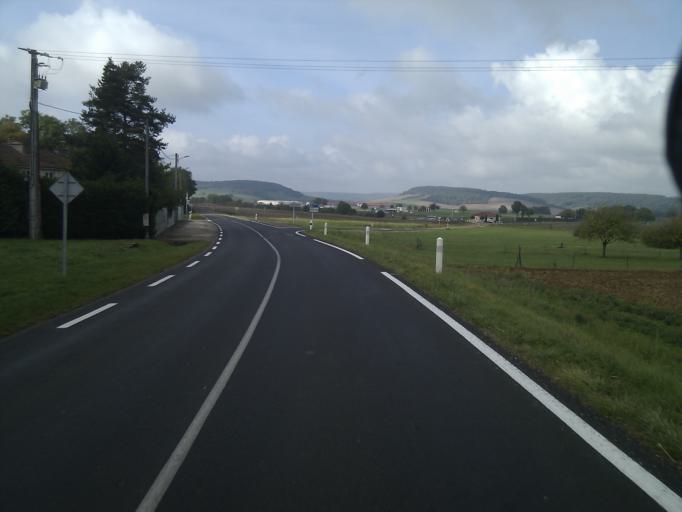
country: FR
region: Champagne-Ardenne
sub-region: Departement de la Haute-Marne
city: Chateauvillain
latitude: 48.0750
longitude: 4.9624
